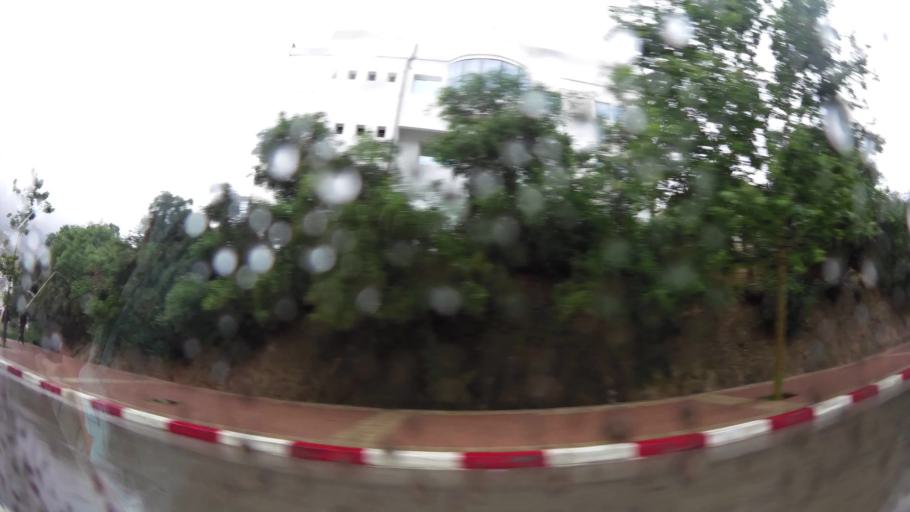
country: MA
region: Taza-Al Hoceima-Taounate
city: Al Hoceima
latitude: 35.2358
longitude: -3.9260
